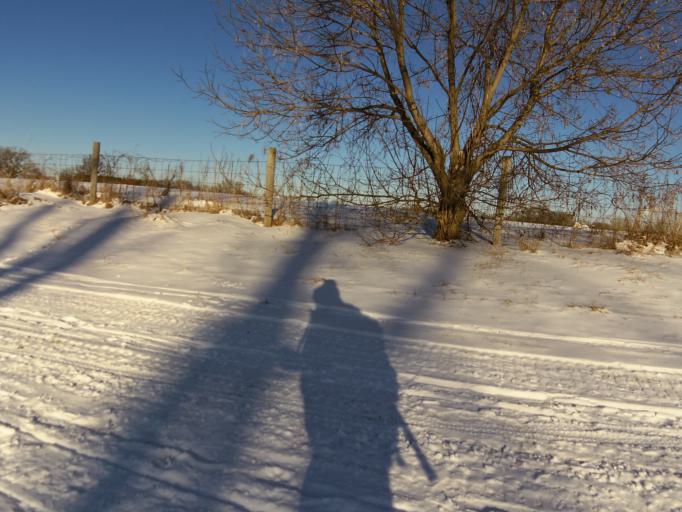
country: US
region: Minnesota
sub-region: Washington County
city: Lake Elmo
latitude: 44.9910
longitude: -92.9126
